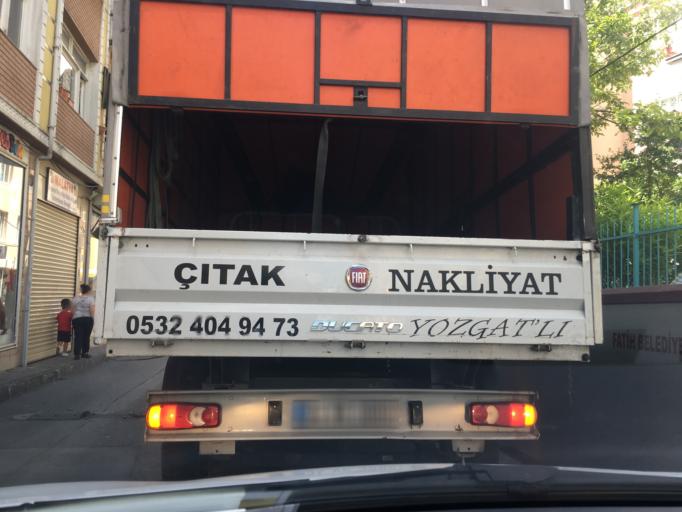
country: TR
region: Istanbul
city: Istanbul
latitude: 41.0010
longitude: 28.9296
